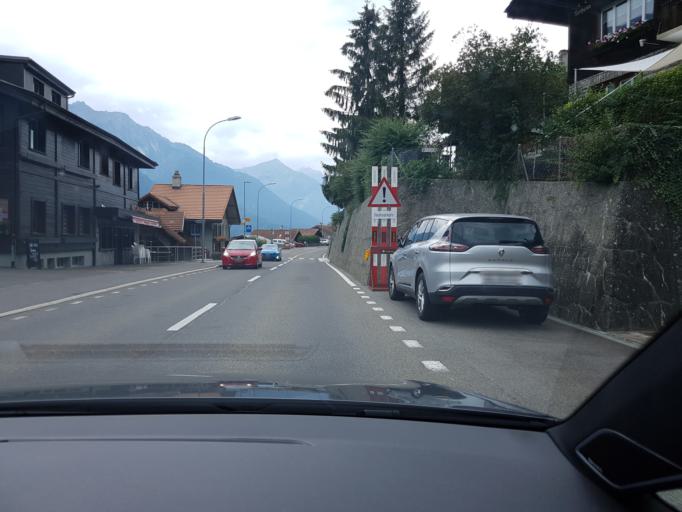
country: CH
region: Bern
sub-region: Interlaken-Oberhasli District
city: Ringgenberg
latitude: 46.7178
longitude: 7.9296
